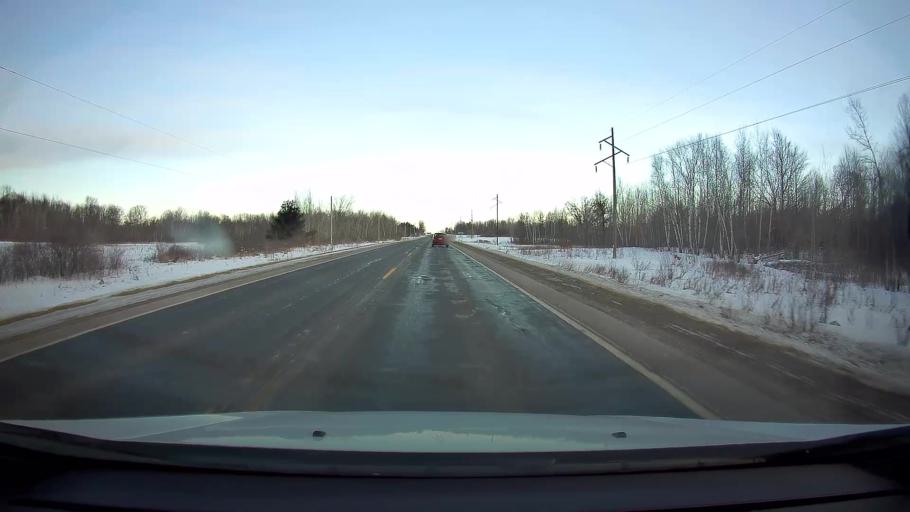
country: US
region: Wisconsin
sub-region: Barron County
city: Turtle Lake
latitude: 45.3563
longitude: -92.1669
